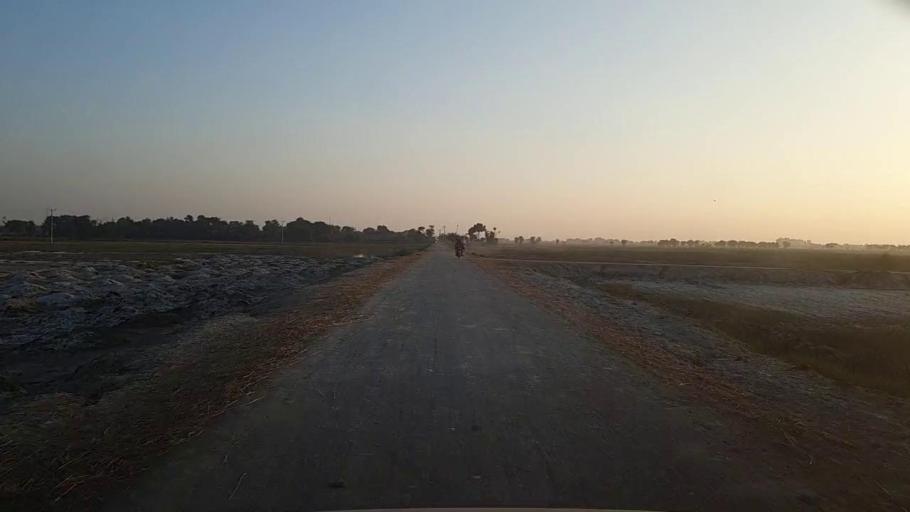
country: PK
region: Sindh
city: Khairpur Nathan Shah
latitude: 27.1737
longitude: 67.7335
